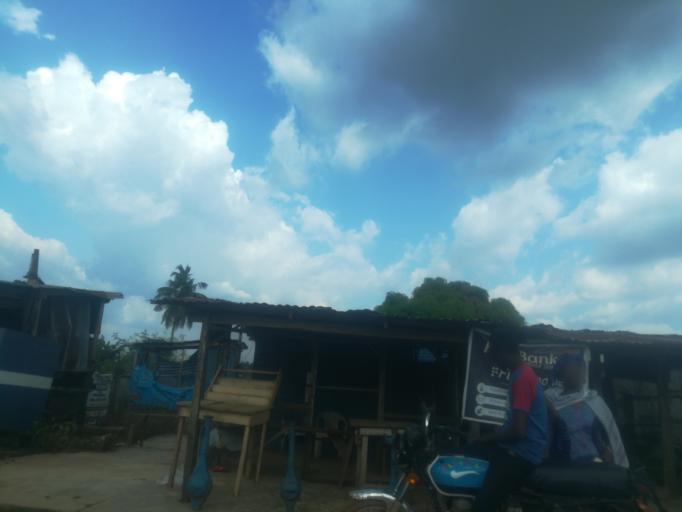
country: NG
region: Oyo
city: Ibadan
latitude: 7.3990
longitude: 3.8359
